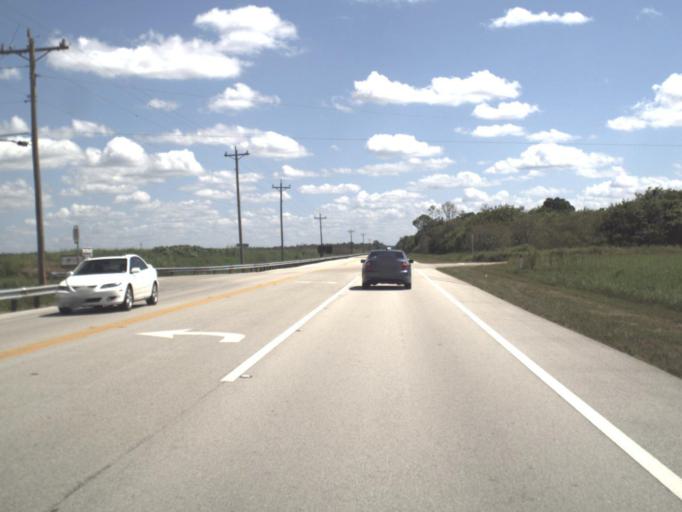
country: US
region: Florida
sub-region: Collier County
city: Lely Resort
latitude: 26.0145
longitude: -81.6229
